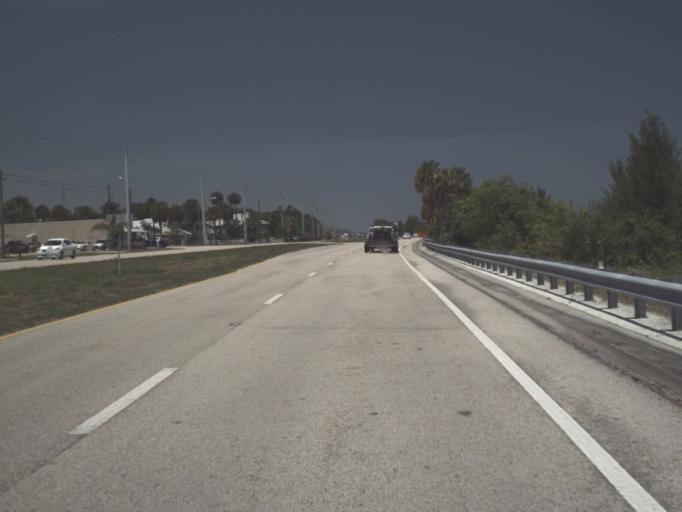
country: US
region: Florida
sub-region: Brevard County
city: Micco
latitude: 27.8739
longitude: -80.4977
